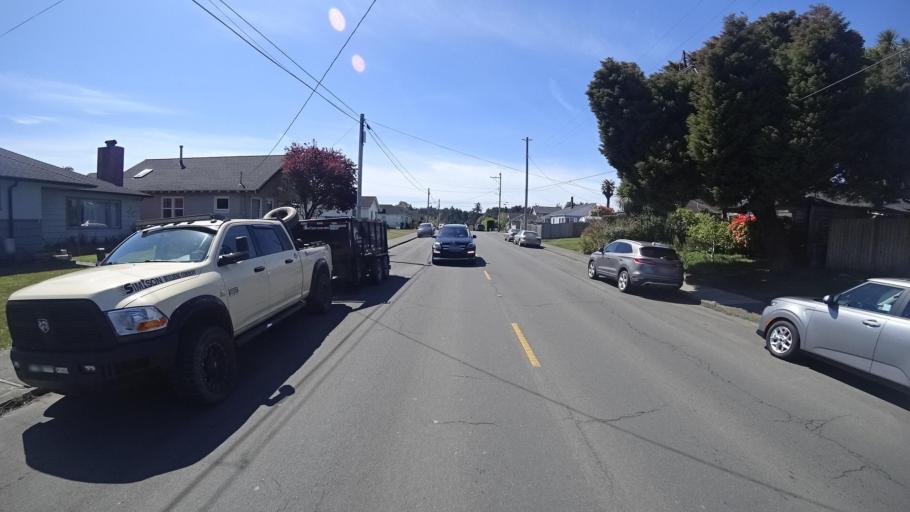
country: US
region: California
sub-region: Humboldt County
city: Eureka
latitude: 40.7945
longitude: -124.1481
